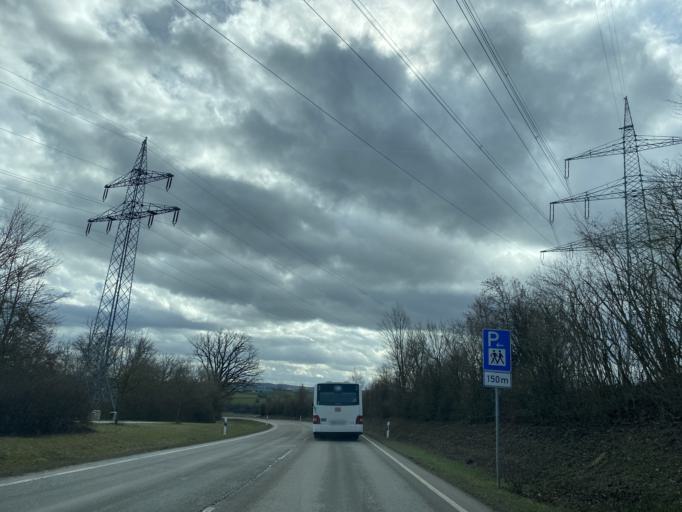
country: DE
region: Baden-Wuerttemberg
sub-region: Regierungsbezirk Stuttgart
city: Hemmingen
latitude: 48.8473
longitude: 8.9970
